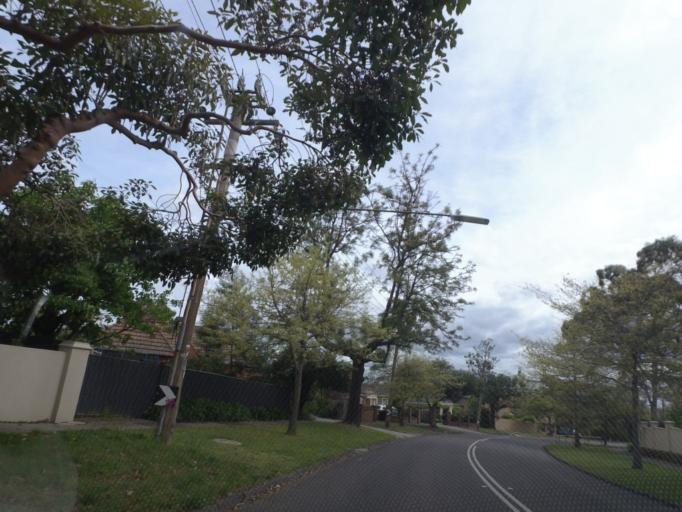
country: AU
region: Victoria
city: Mont Albert
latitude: -37.8099
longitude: 145.0884
